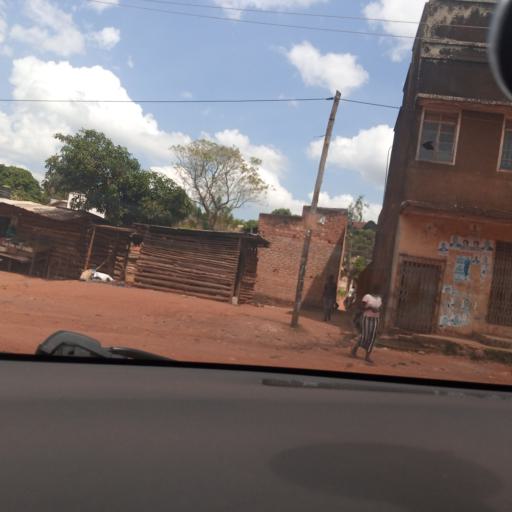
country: UG
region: Central Region
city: Masaka
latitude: -0.3299
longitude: 31.7395
